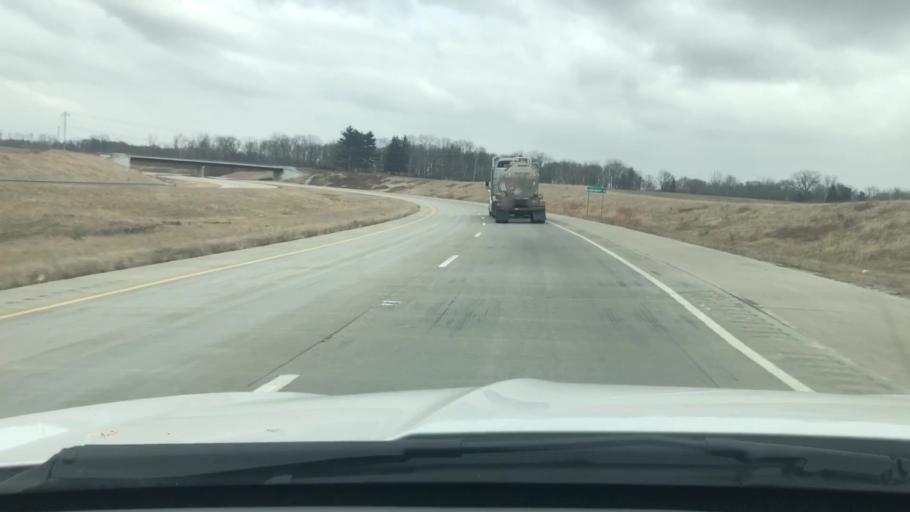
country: US
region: Indiana
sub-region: Carroll County
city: Delphi
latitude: 40.5730
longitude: -86.6481
